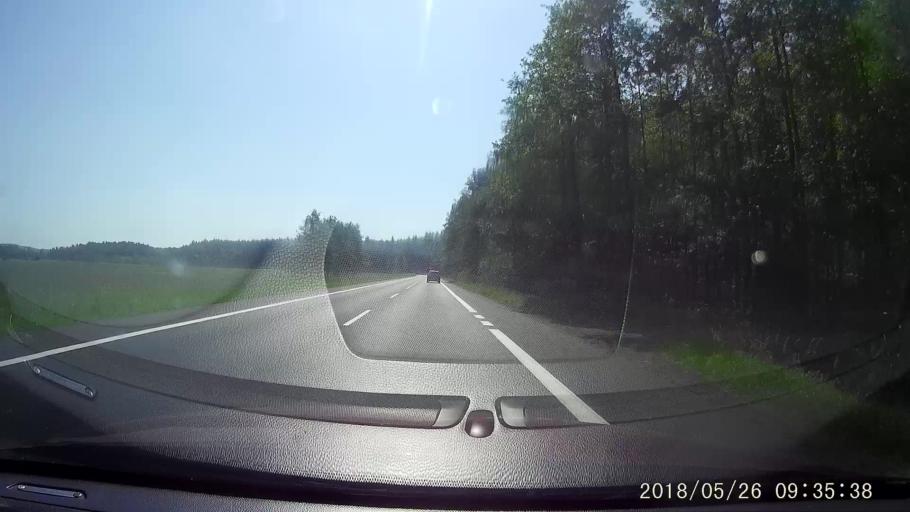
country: PL
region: Lower Silesian Voivodeship
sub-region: Powiat zgorzelecki
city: Lagow
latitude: 51.1560
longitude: 15.0678
